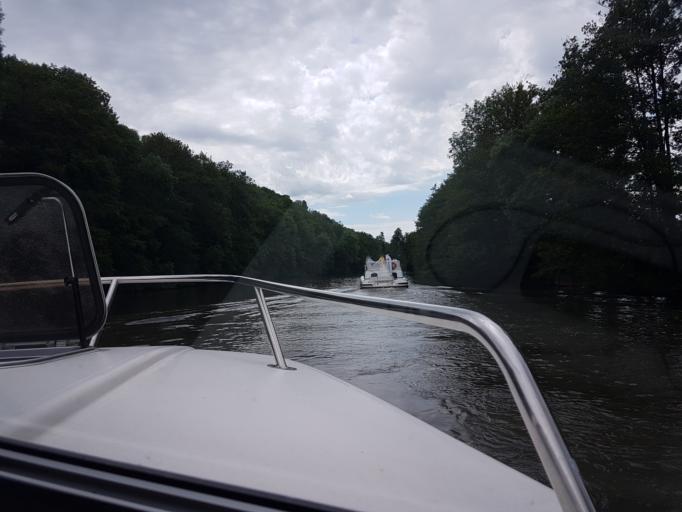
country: FR
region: Bourgogne
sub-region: Departement de la Nievre
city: Clamecy
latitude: 47.4675
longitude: 3.5283
